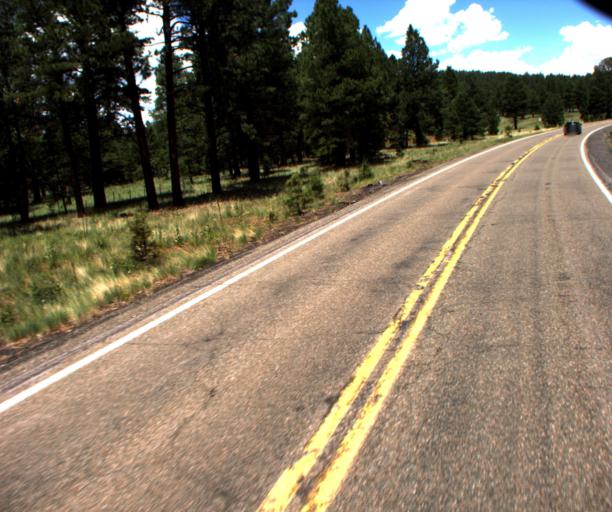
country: US
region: Arizona
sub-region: Coconino County
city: Parks
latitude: 35.3763
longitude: -111.7896
